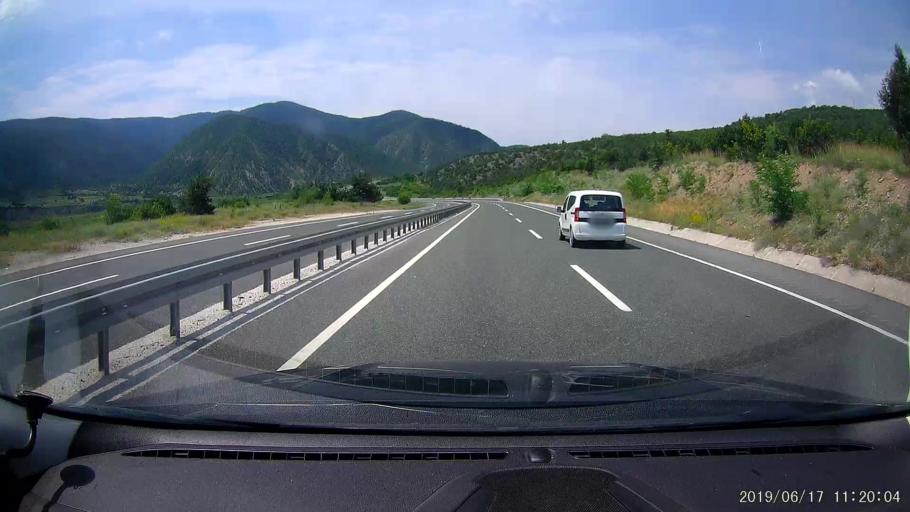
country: TR
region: Cankiri
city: Yaprakli
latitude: 40.9179
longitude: 33.8143
